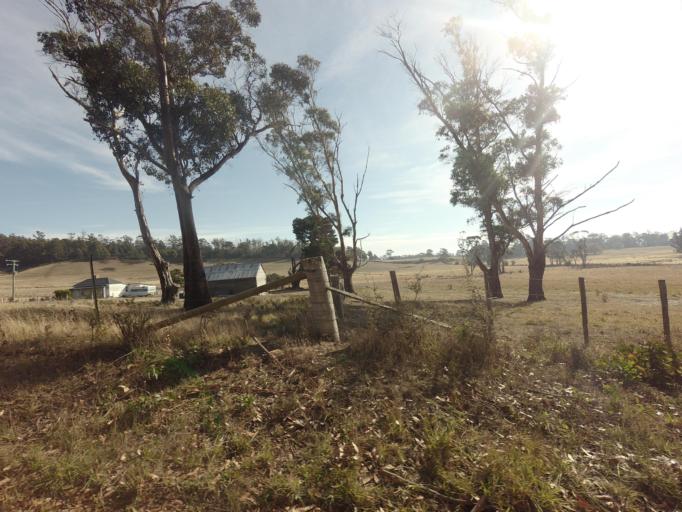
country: AU
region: Tasmania
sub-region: Sorell
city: Sorell
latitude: -42.4804
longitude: 147.4806
